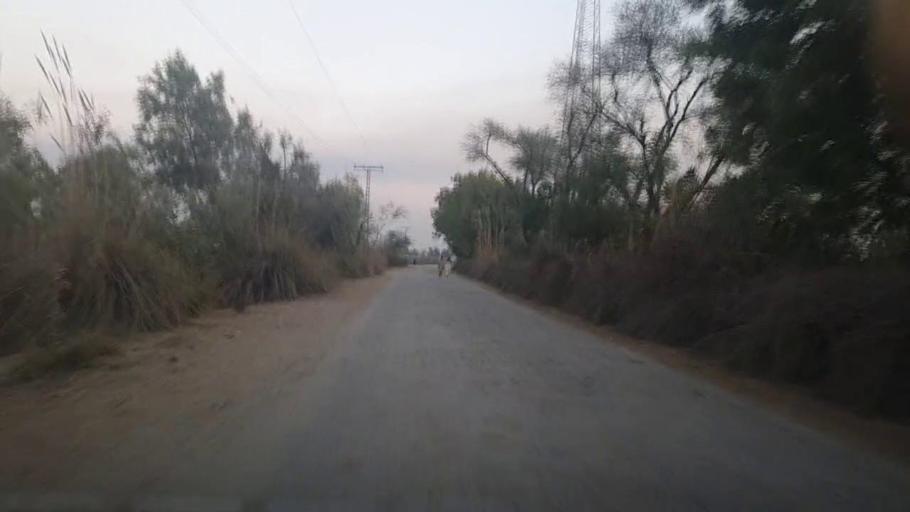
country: PK
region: Sindh
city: Kandiari
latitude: 26.6834
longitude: 68.9379
